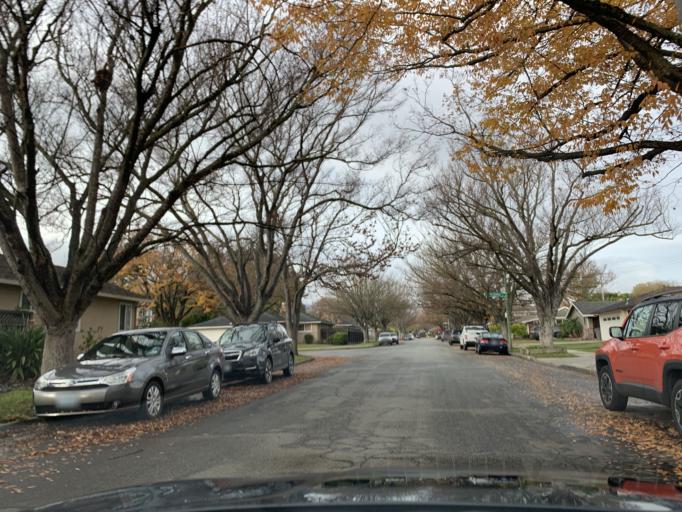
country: US
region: California
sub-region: Santa Clara County
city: Cambrian Park
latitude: 37.2503
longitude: -121.9462
